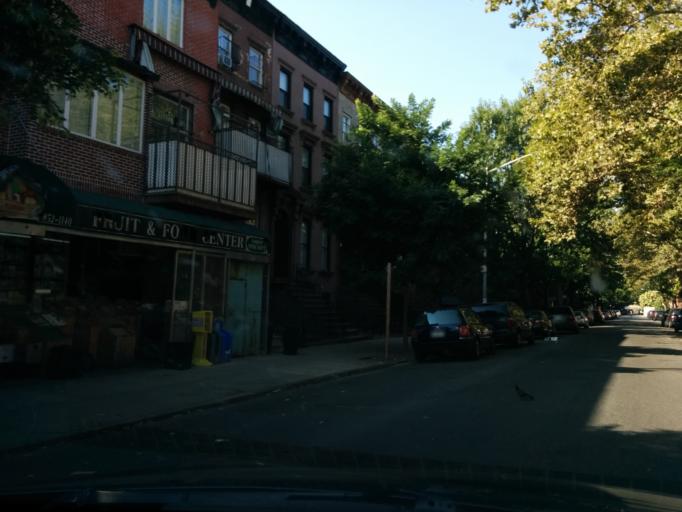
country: US
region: New York
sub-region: Queens County
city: Long Island City
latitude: 40.7029
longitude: -73.9571
